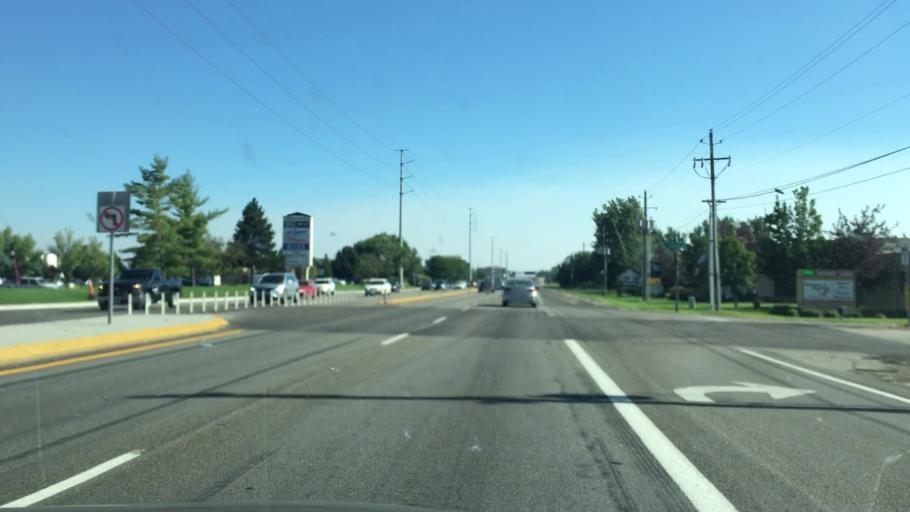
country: US
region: Idaho
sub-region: Ada County
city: Meridian
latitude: 43.6169
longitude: -116.3547
